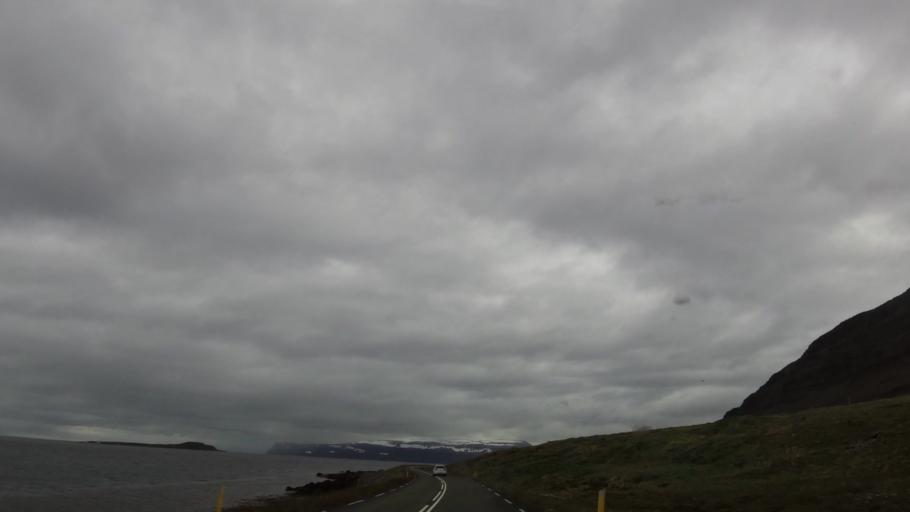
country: IS
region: Westfjords
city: Isafjoerdur
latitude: 66.0210
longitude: -22.7802
